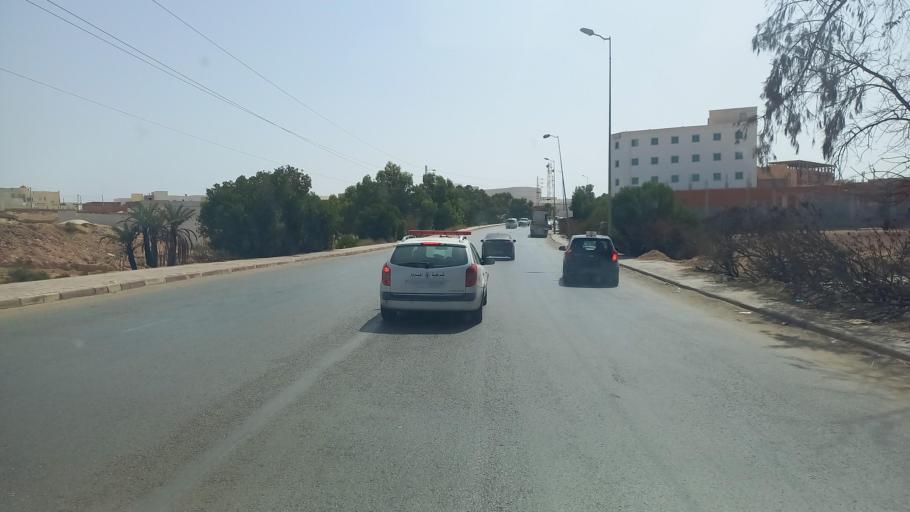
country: TN
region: Madanin
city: Medenine
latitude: 33.3446
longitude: 10.5002
